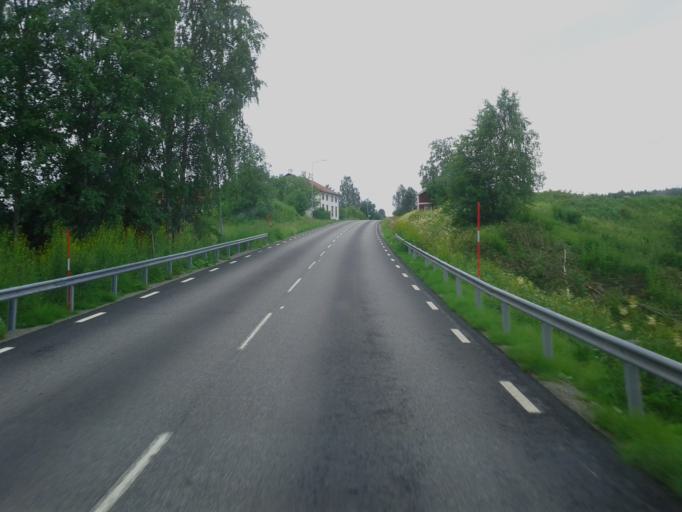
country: SE
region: Vaesterbotten
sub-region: Skelleftea Kommun
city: Viken
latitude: 64.8805
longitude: 20.7812
